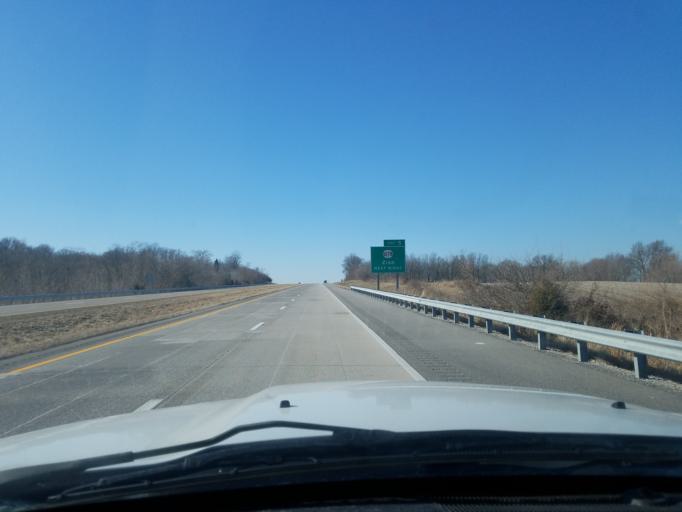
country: US
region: Kentucky
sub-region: Henderson County
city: Henderson
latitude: 37.7823
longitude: -87.4598
